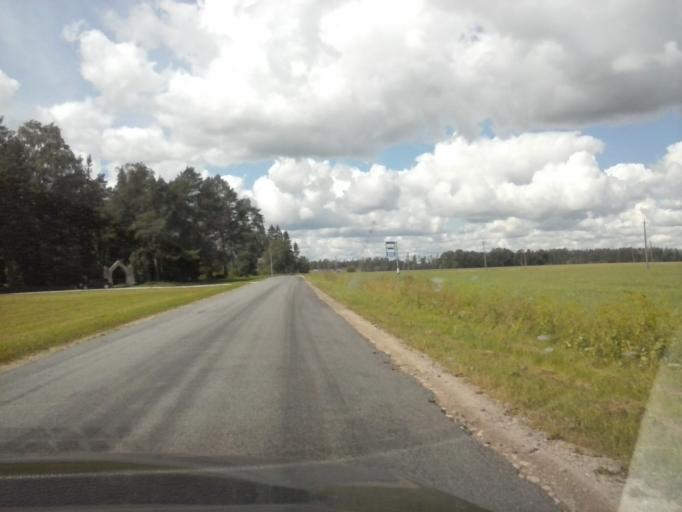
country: EE
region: Laeaene-Virumaa
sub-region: Rakke vald
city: Rakke
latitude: 59.0486
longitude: 26.3787
